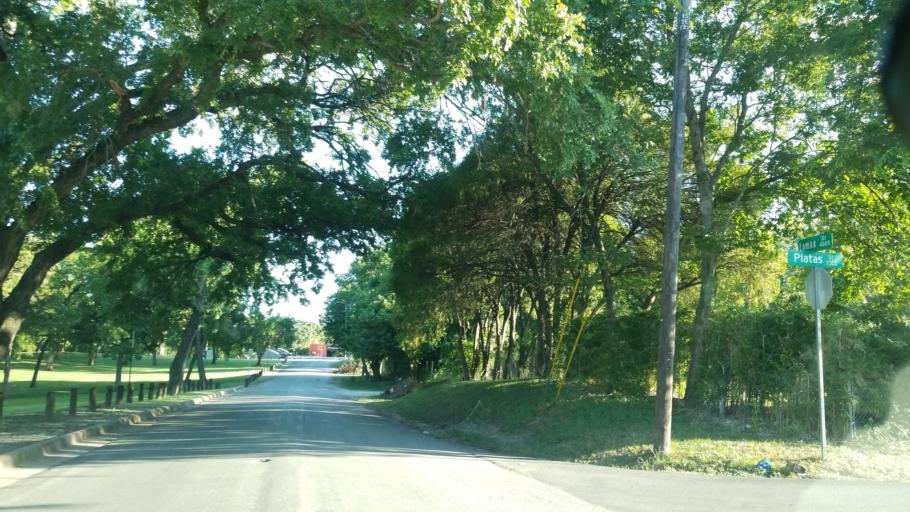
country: US
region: Texas
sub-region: Dallas County
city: Balch Springs
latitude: 32.7730
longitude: -96.6944
